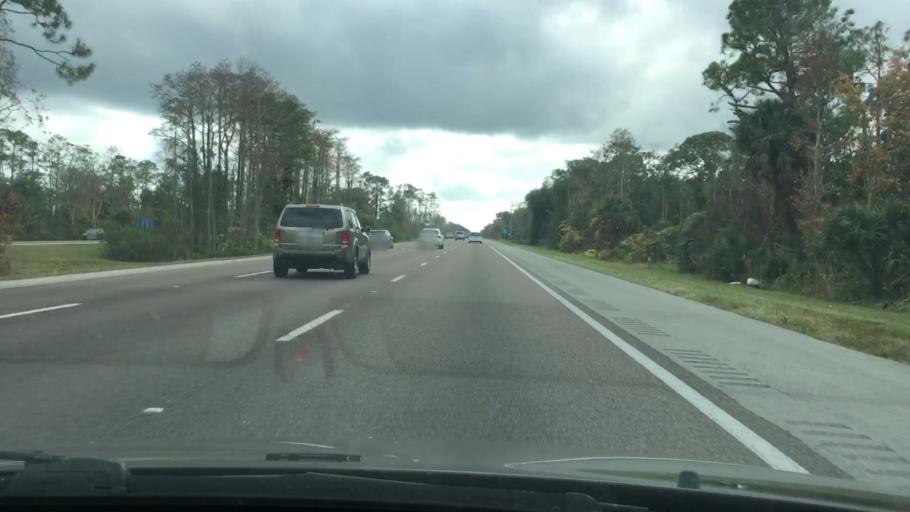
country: US
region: Florida
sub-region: Volusia County
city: Glencoe
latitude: 29.0025
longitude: -80.9815
